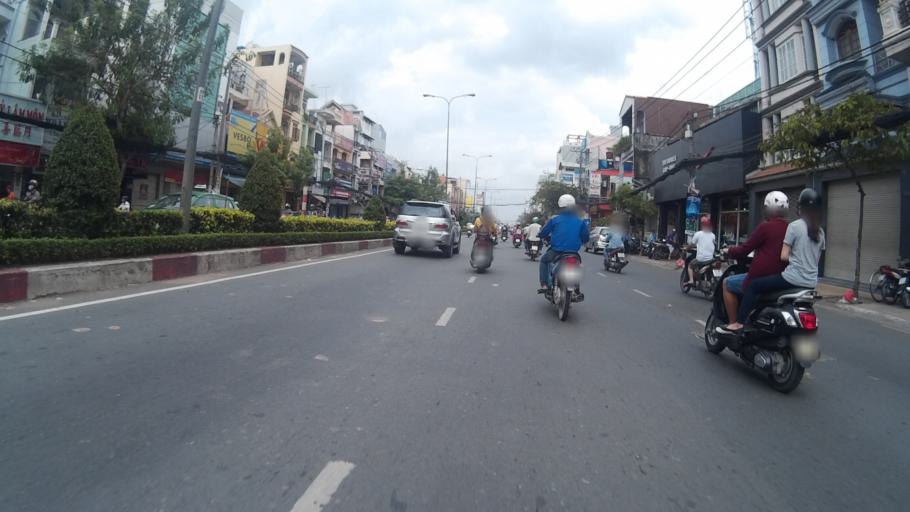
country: VN
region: Ho Chi Minh City
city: Quan Tan Phu
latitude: 10.8021
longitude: 106.6429
